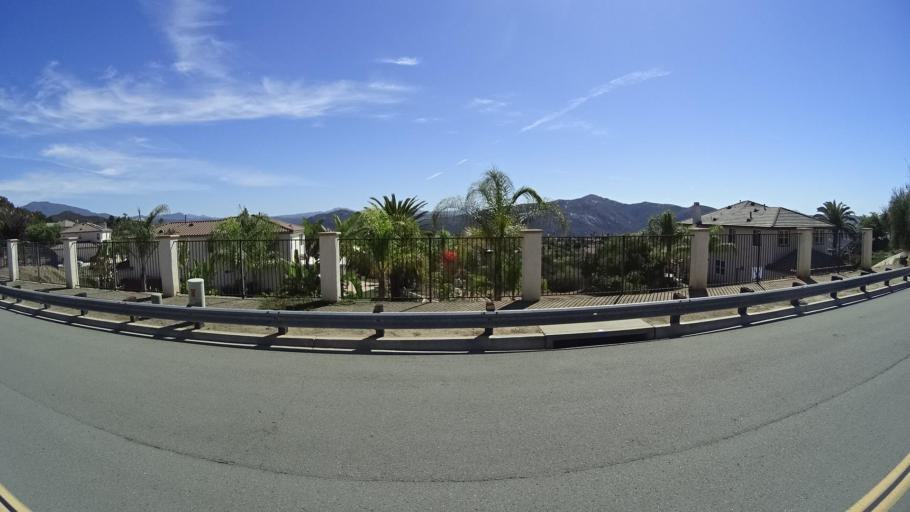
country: US
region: California
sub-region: San Diego County
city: Harbison Canyon
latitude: 32.8796
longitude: -116.8421
